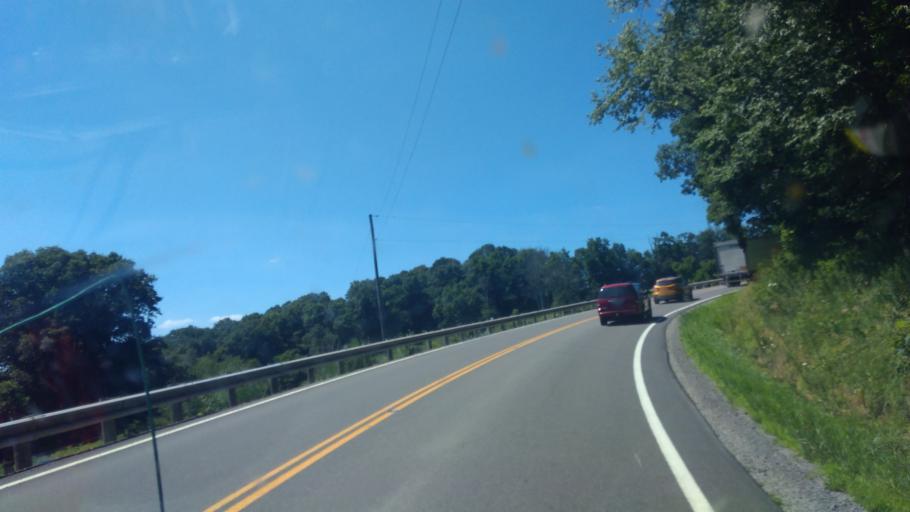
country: US
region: Ohio
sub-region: Carroll County
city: Carrollton
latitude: 40.5059
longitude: -80.9870
